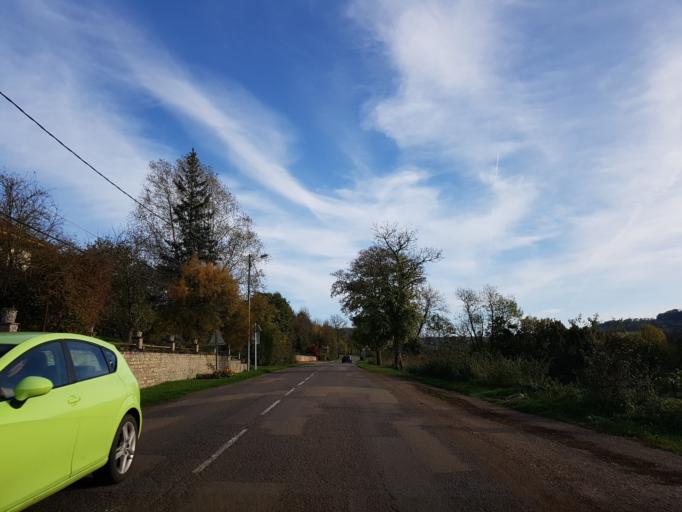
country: FR
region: Bourgogne
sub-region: Departement de la Cote-d'Or
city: Pouilly-en-Auxois
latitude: 47.3179
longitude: 4.6002
